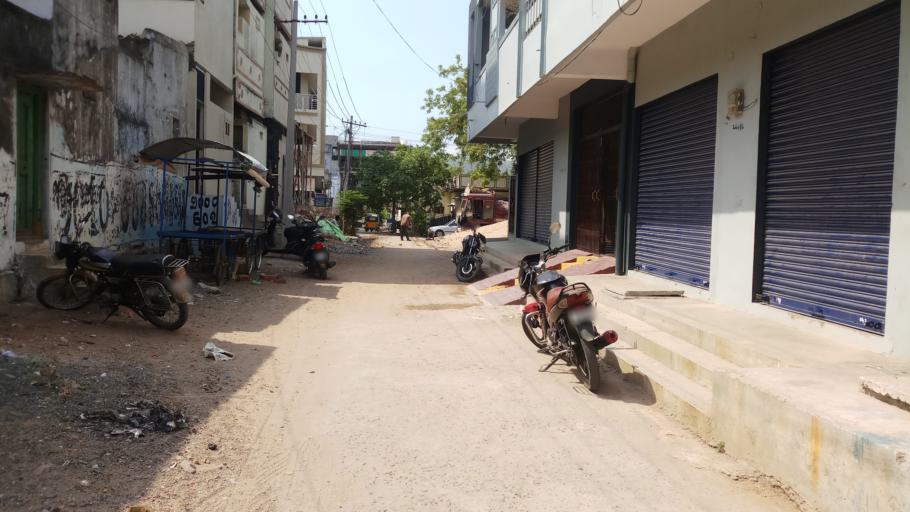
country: IN
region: Telangana
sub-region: Khammam
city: Paloncha
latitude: 17.6003
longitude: 80.7002
